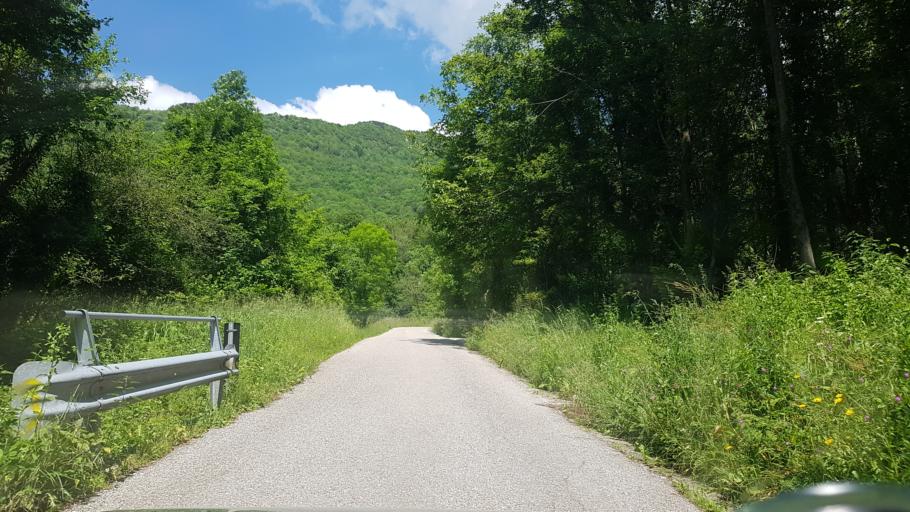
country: IT
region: Friuli Venezia Giulia
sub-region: Provincia di Udine
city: Torreano
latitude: 46.1684
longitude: 13.4279
